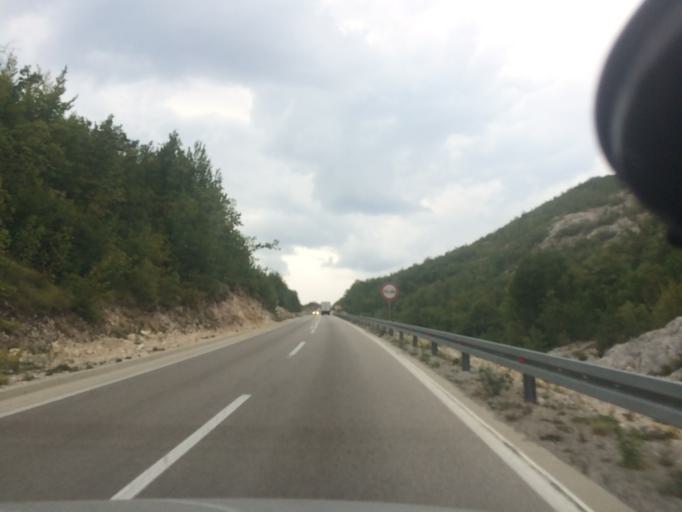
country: ME
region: Kotor
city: Risan
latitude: 42.6786
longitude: 18.6405
